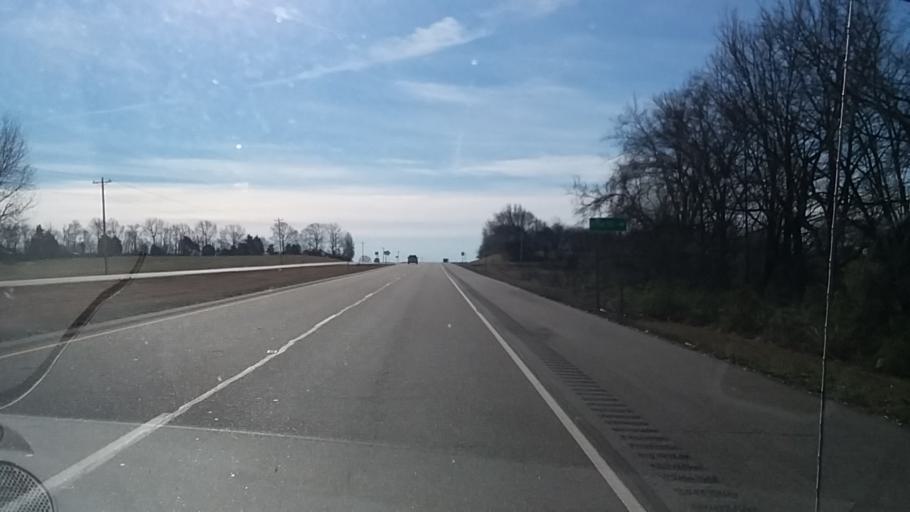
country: US
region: Tennessee
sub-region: Lauderdale County
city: Halls
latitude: 35.8942
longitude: -89.2403
